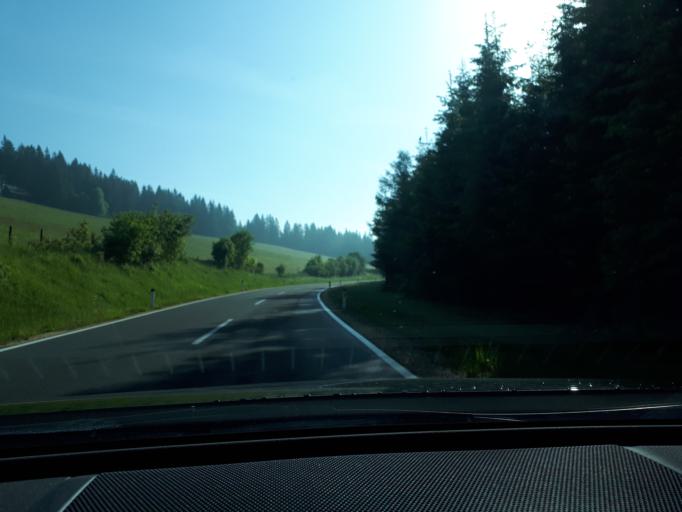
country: AT
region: Styria
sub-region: Politischer Bezirk Voitsberg
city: Pack
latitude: 46.9641
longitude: 14.9699
